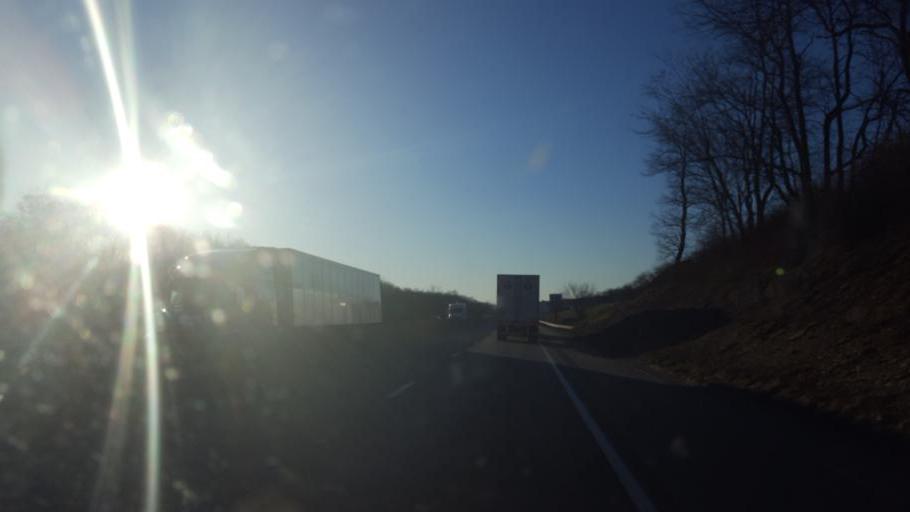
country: US
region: Pennsylvania
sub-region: Washington County
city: Ellsworth
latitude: 40.1570
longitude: -80.0402
